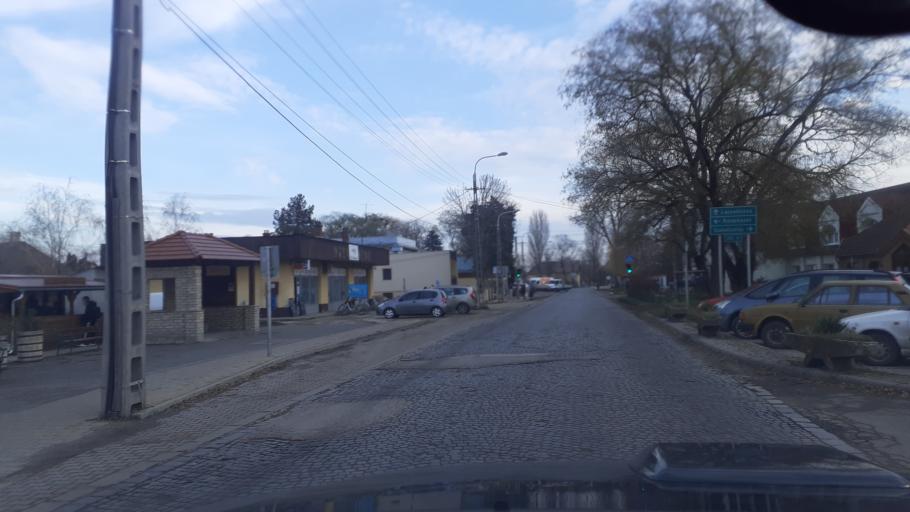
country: HU
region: Bacs-Kiskun
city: Kunszentmiklos
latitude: 47.0262
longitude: 19.1238
